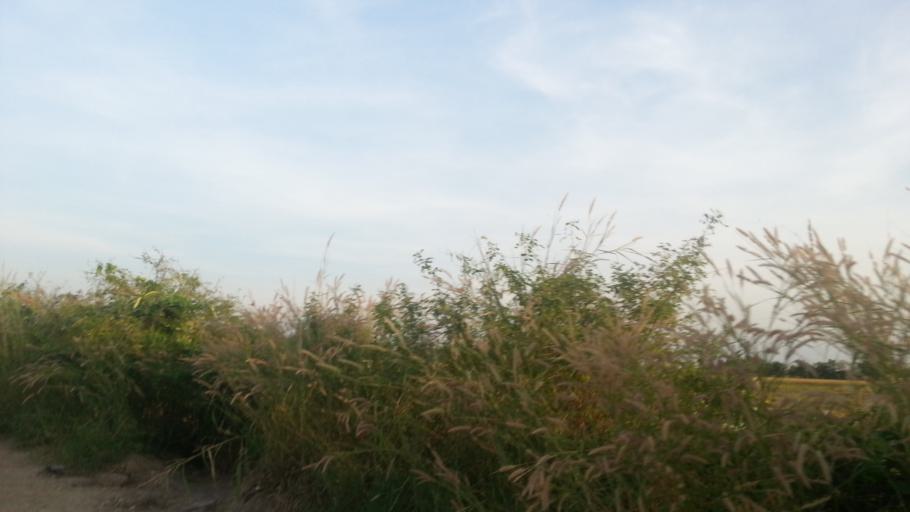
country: TH
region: Pathum Thani
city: Ban Lam Luk Ka
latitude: 14.0351
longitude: 100.8543
